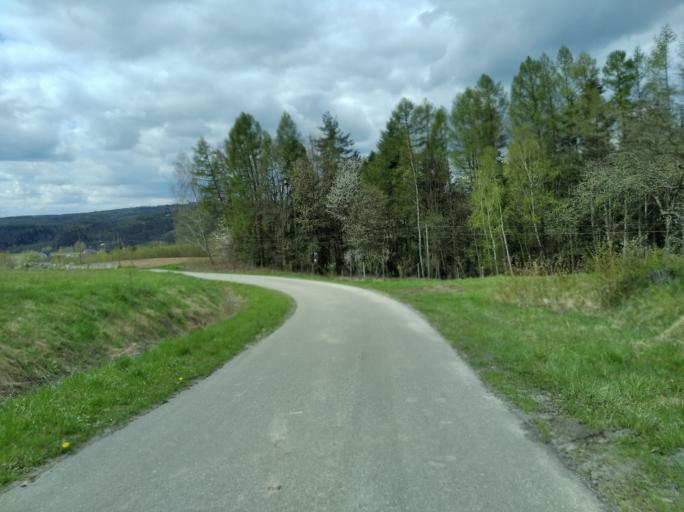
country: PL
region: Subcarpathian Voivodeship
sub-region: Powiat strzyzowski
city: Niebylec
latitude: 49.8826
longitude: 21.9224
